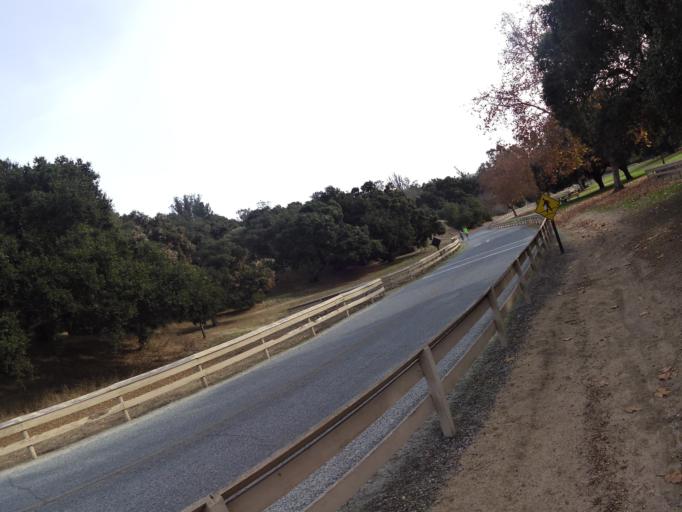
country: US
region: California
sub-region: Monterey County
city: Salinas
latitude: 36.6006
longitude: -121.6931
